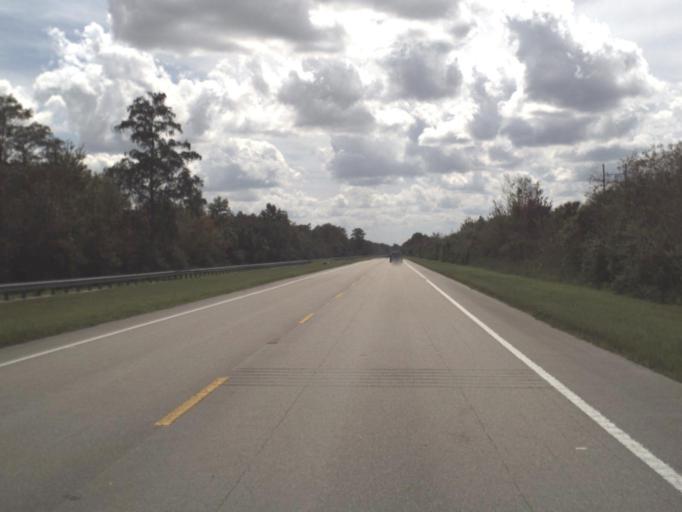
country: US
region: Florida
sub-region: Collier County
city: Orangetree
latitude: 26.0693
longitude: -81.3446
